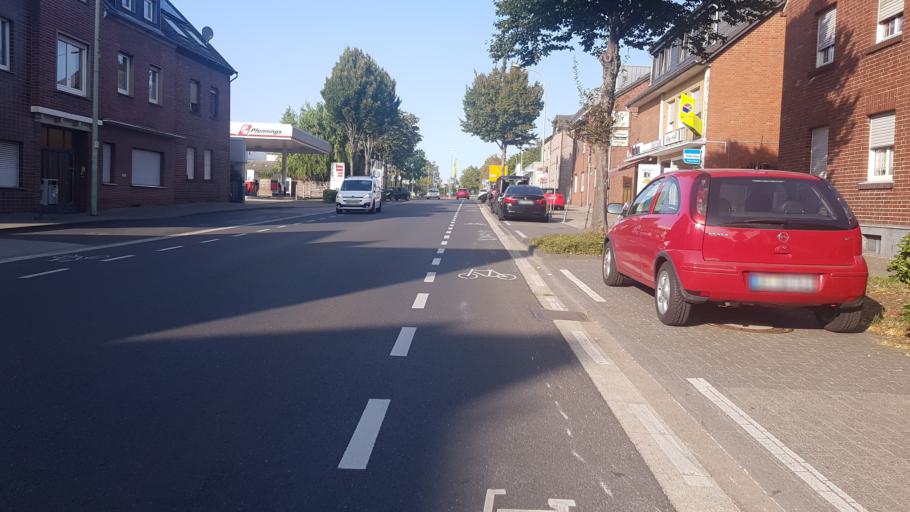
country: DE
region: North Rhine-Westphalia
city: Baesweiler
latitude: 50.9094
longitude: 6.1905
